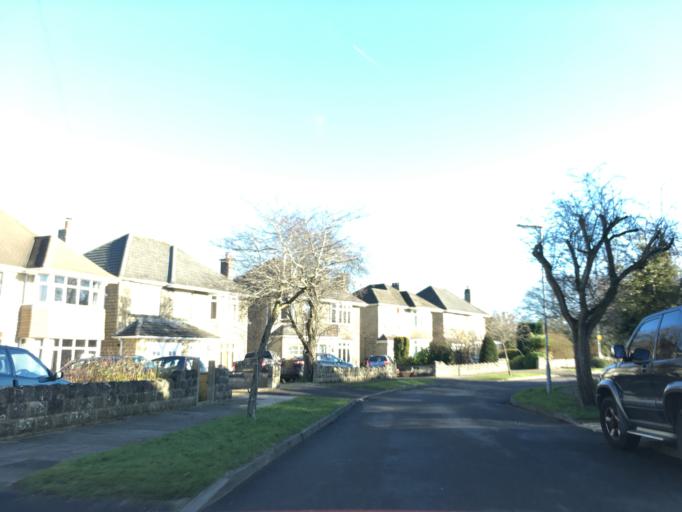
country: GB
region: England
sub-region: Borough of Swindon
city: Swindon
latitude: 51.5491
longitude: -1.7682
